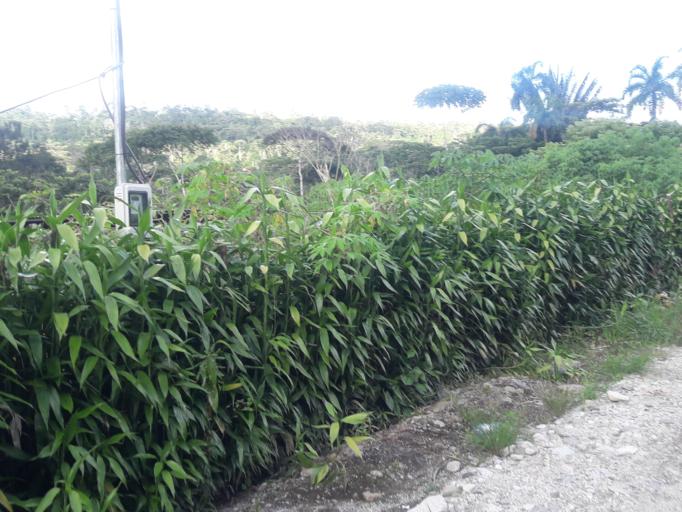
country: EC
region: Napo
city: Tena
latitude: -0.9702
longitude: -77.8409
